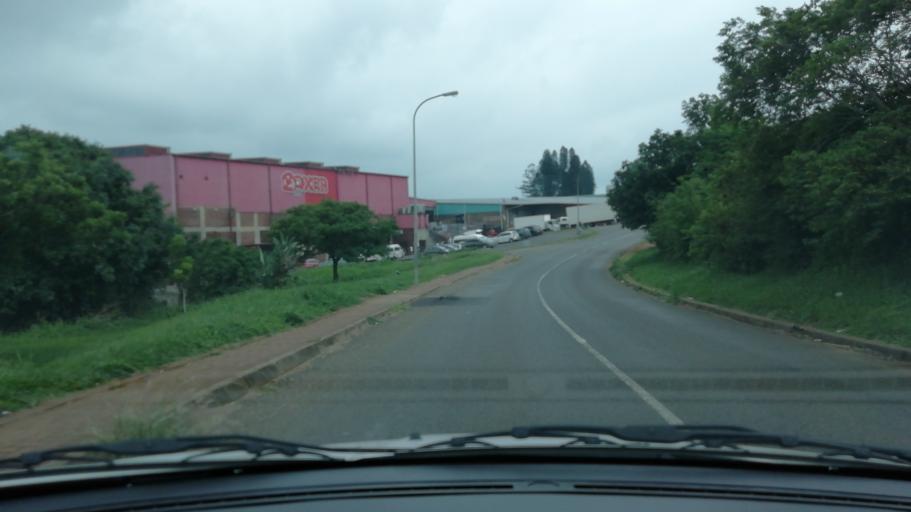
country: ZA
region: KwaZulu-Natal
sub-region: uThungulu District Municipality
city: Empangeni
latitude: -28.7457
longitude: 31.8849
